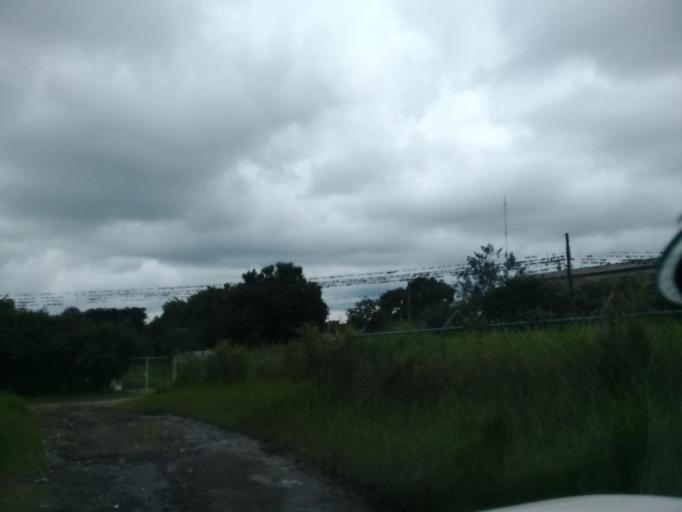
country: MX
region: Veracruz
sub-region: Emiliano Zapata
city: Dos Rios
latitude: 19.4817
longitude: -96.7950
